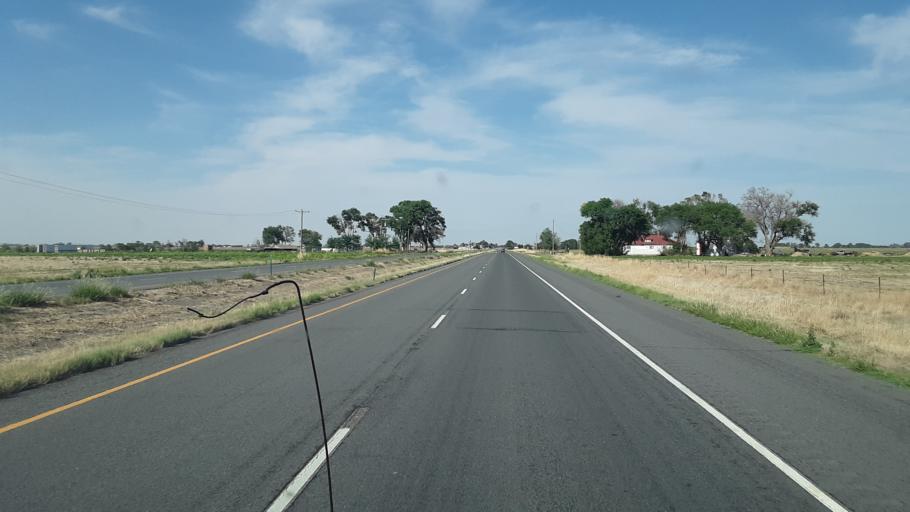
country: US
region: Colorado
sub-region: Bent County
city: Las Animas
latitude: 38.0897
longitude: -103.1726
